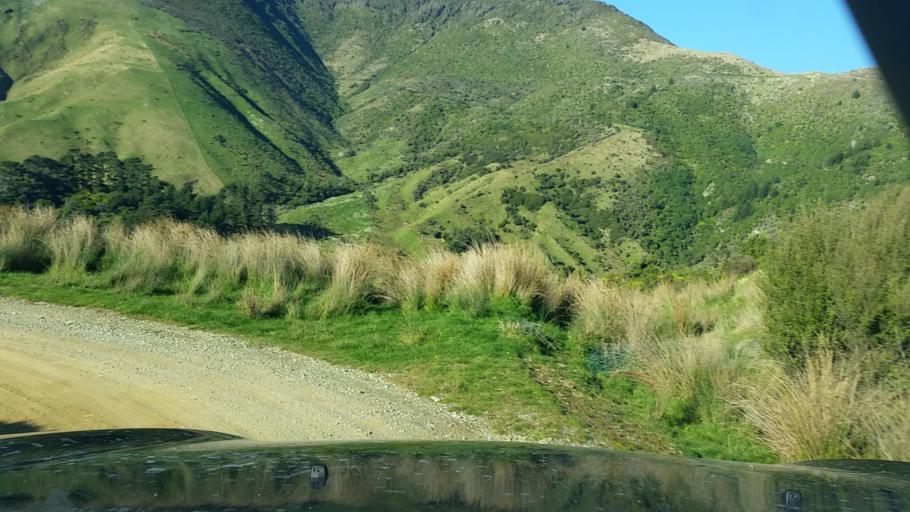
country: NZ
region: Marlborough
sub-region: Marlborough District
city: Picton
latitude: -41.0212
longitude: 174.1426
